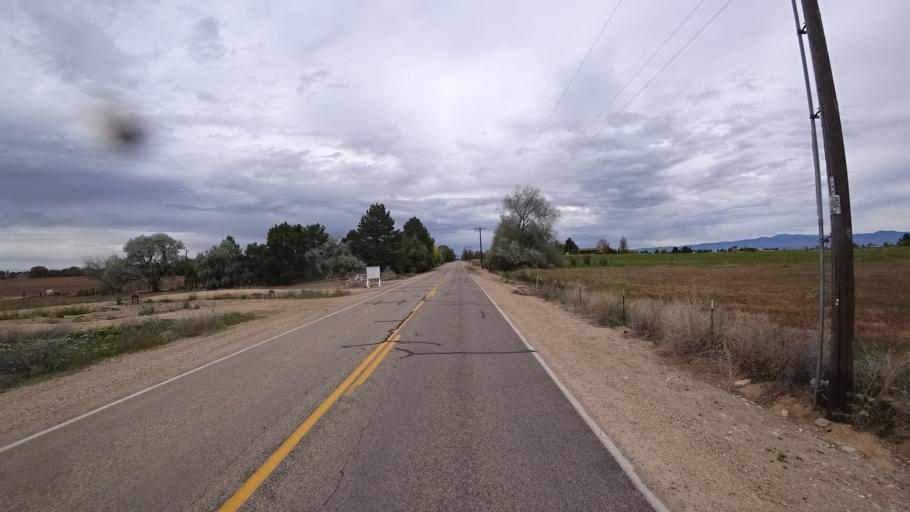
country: US
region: Idaho
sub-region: Ada County
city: Kuna
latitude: 43.5494
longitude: -116.4139
